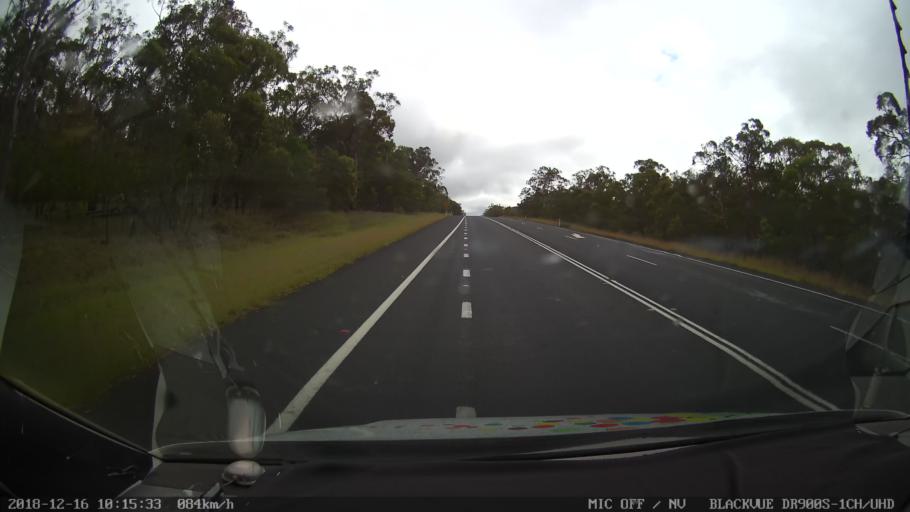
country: AU
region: New South Wales
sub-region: Tenterfield Municipality
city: Carrolls Creek
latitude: -29.2764
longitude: 151.9738
